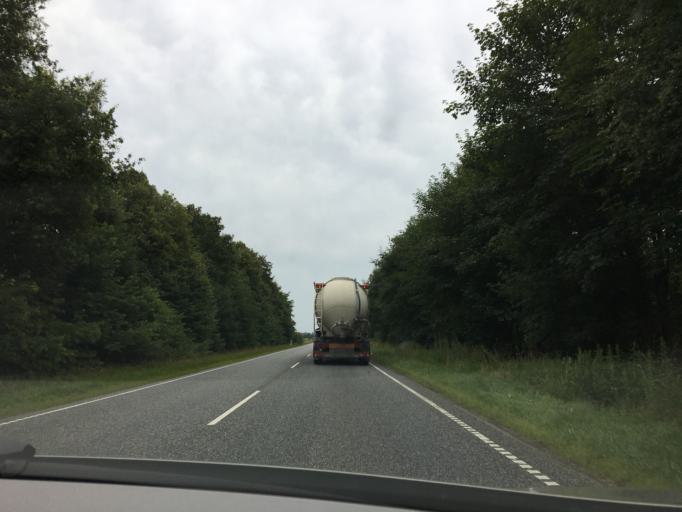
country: DK
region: Central Jutland
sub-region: Herning Kommune
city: Sunds
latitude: 56.3163
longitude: 8.9940
